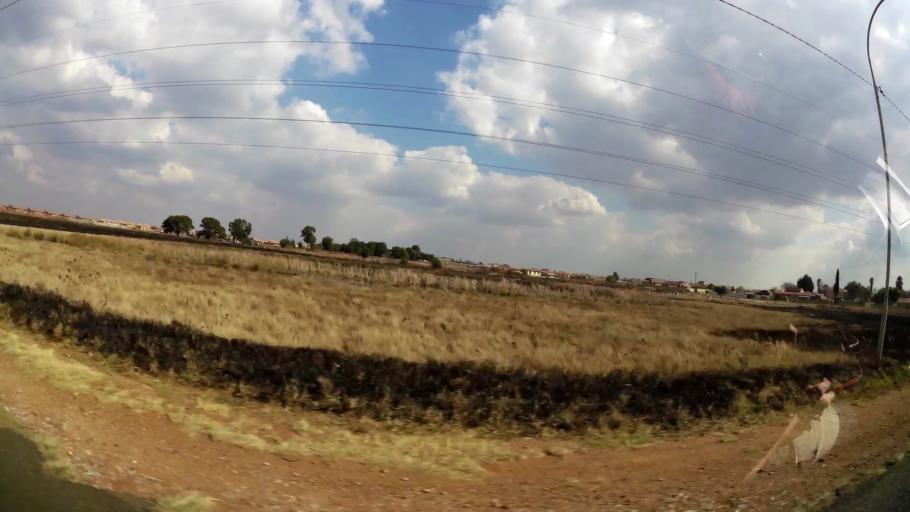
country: ZA
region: Gauteng
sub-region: Ekurhuleni Metropolitan Municipality
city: Benoni
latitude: -26.1235
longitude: 28.3817
